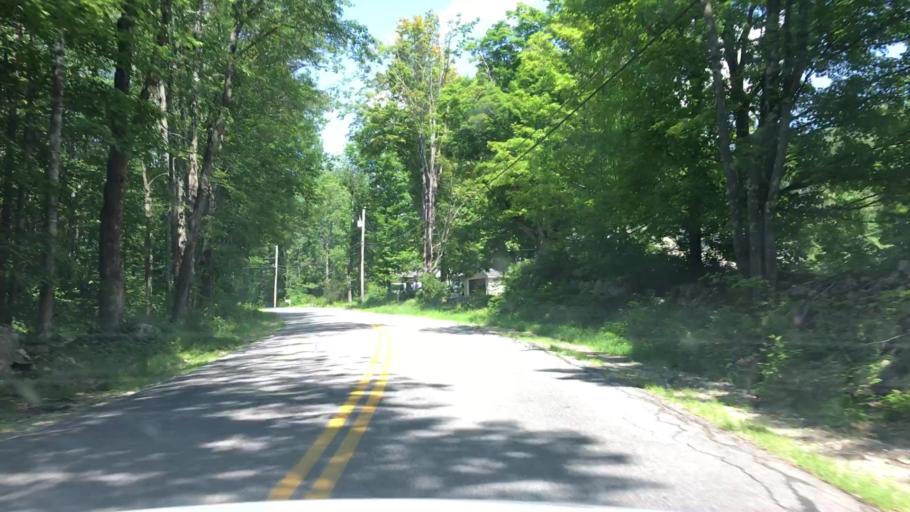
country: US
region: Maine
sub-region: Cumberland County
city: Raymond
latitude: 43.9407
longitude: -70.5230
